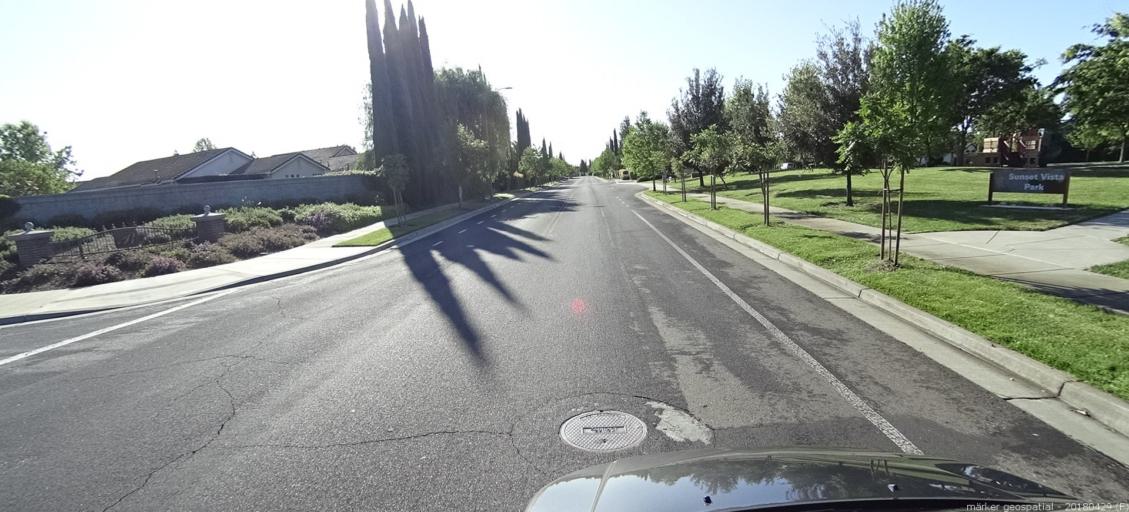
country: US
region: California
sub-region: Yolo County
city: West Sacramento
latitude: 38.5385
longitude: -121.5731
